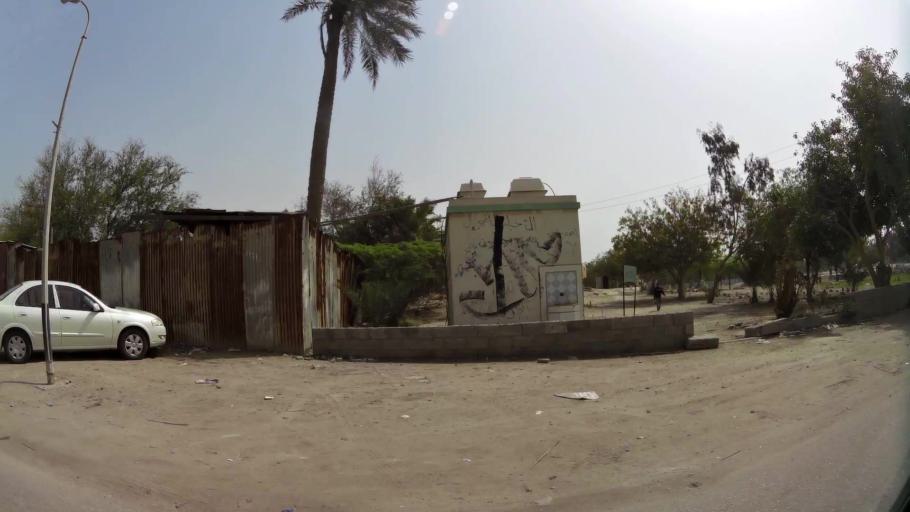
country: BH
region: Manama
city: Jidd Hafs
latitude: 26.2215
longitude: 50.5172
